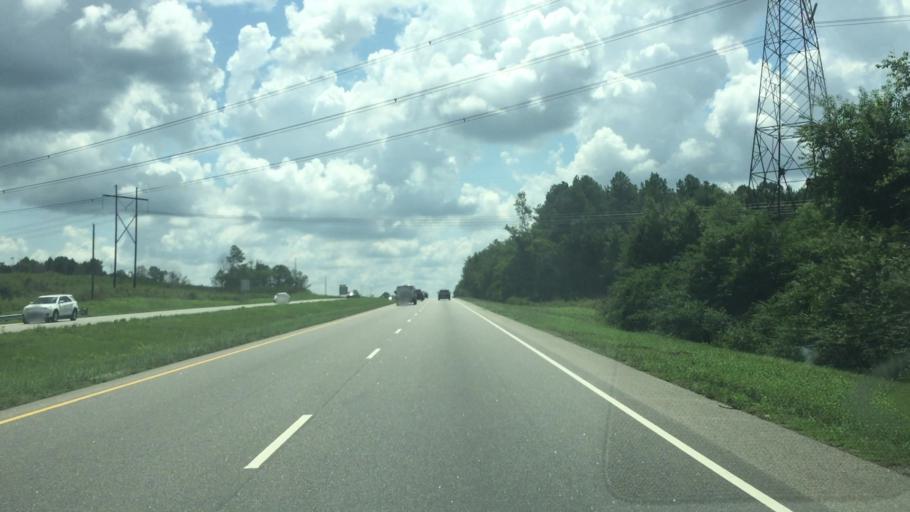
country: US
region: North Carolina
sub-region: Richmond County
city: Hamlet
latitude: 34.8525
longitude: -79.6205
